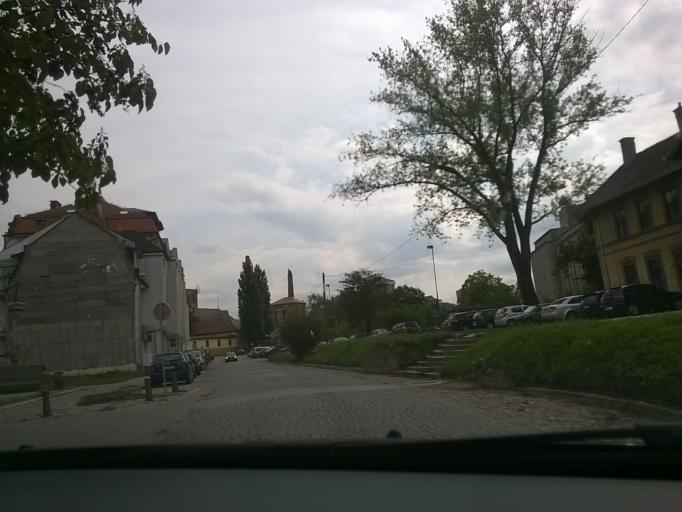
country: RS
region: Autonomna Pokrajina Vojvodina
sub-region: Juznobanatski Okrug
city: Pancevo
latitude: 44.8695
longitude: 20.6371
